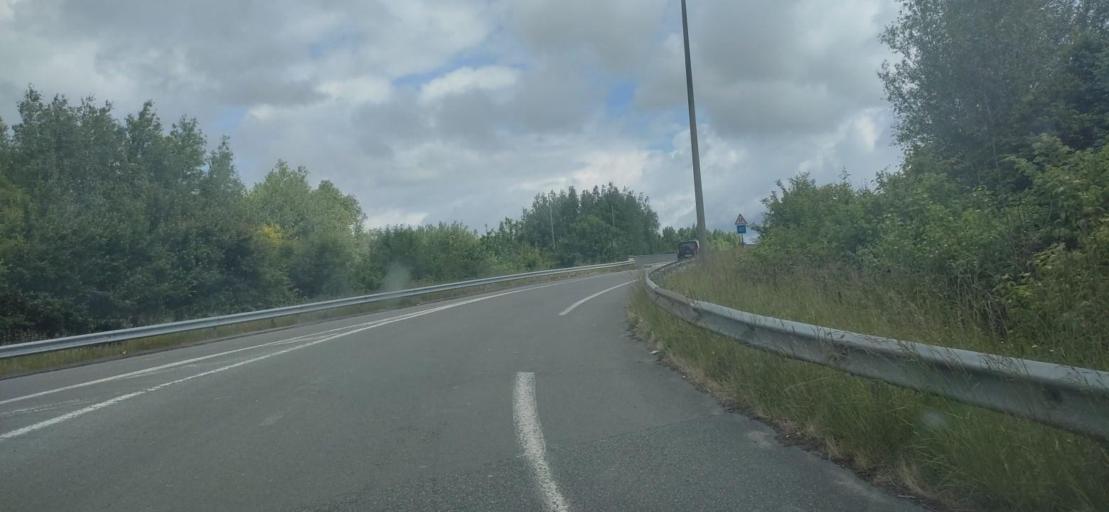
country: FR
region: Nord-Pas-de-Calais
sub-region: Departement du Pas-de-Calais
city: Marck
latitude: 50.9351
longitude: 1.9704
